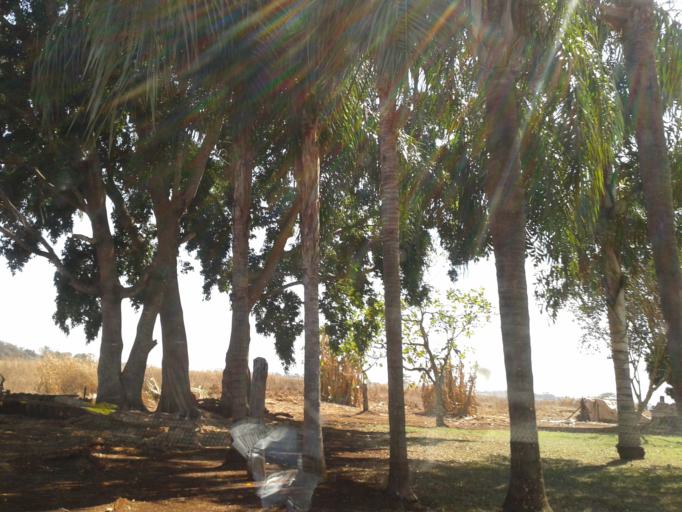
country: BR
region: Minas Gerais
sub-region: Capinopolis
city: Capinopolis
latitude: -18.6142
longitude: -49.4632
